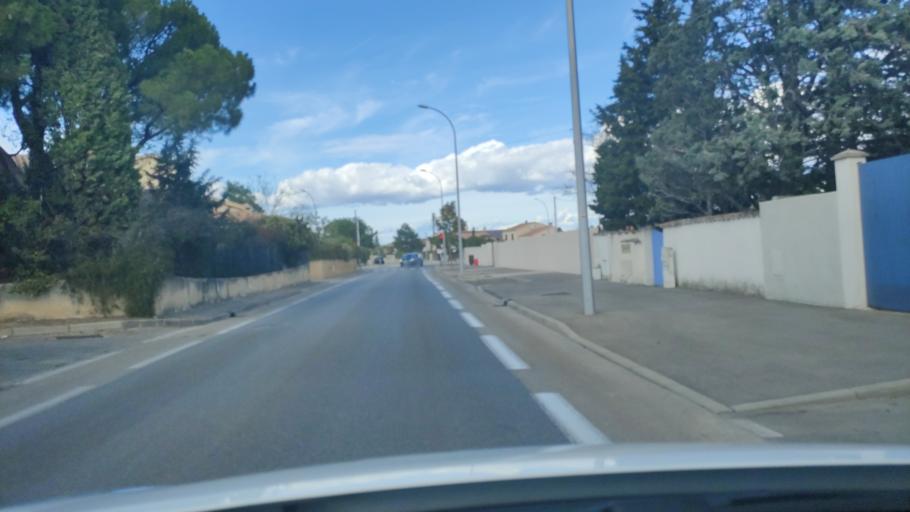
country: FR
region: Languedoc-Roussillon
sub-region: Departement du Gard
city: Villeneuve-les-Avignon
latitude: 43.9739
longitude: 4.7810
